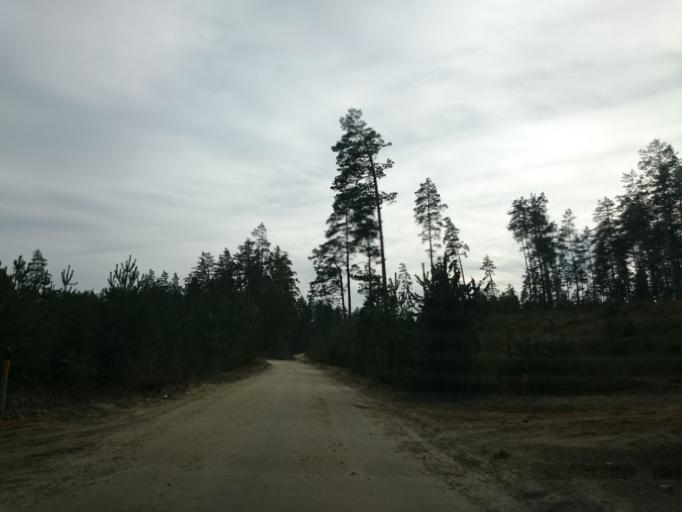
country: LV
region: Garkalne
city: Garkalne
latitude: 57.0298
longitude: 24.3820
